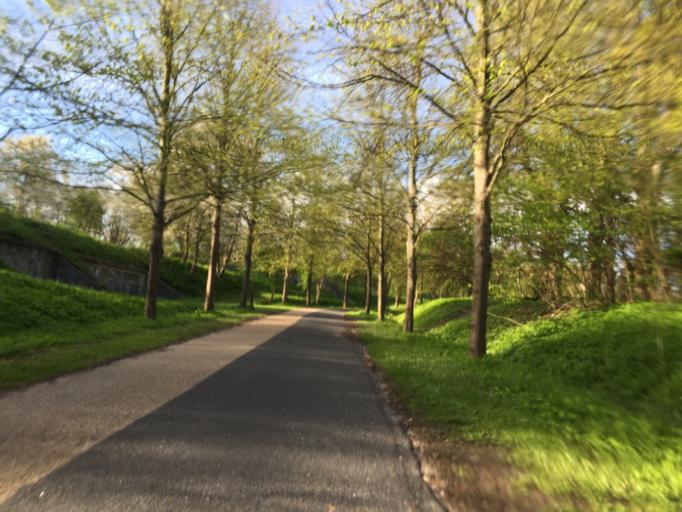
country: DK
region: Capital Region
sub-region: Herlev Kommune
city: Herlev
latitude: 55.7117
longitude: 12.4633
